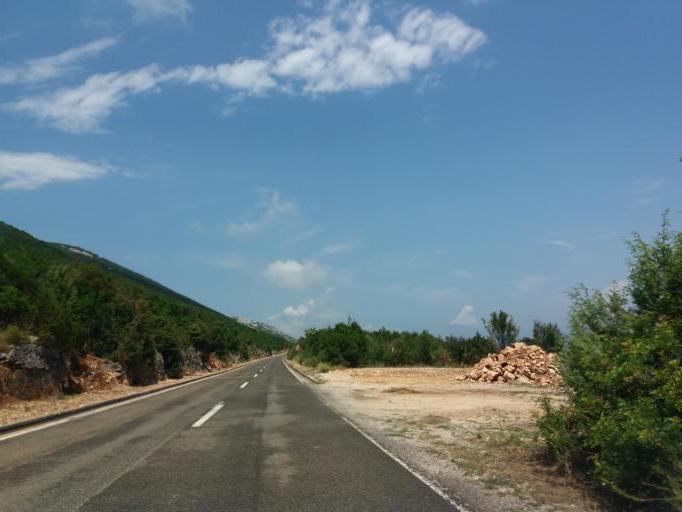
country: HR
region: Zadarska
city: Sali
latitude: 43.9959
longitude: 15.0609
